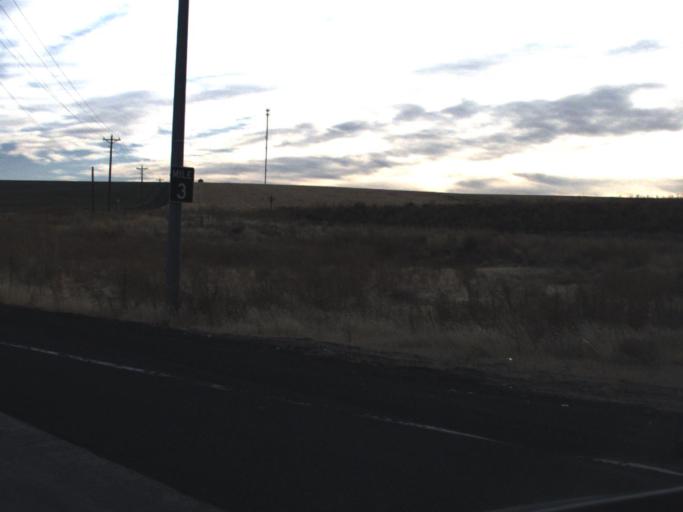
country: US
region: Washington
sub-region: Franklin County
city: Connell
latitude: 46.8229
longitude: -118.6737
